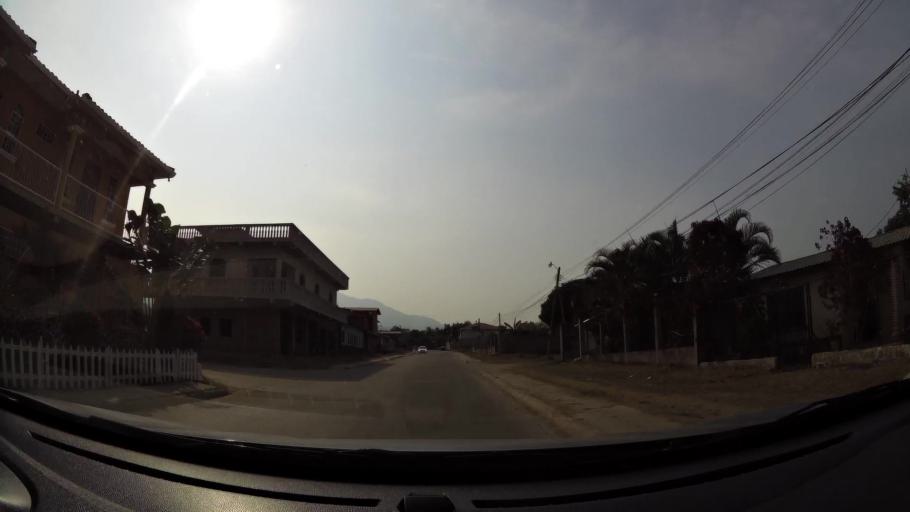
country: HN
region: Comayagua
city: Comayagua
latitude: 14.4512
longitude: -87.6199
